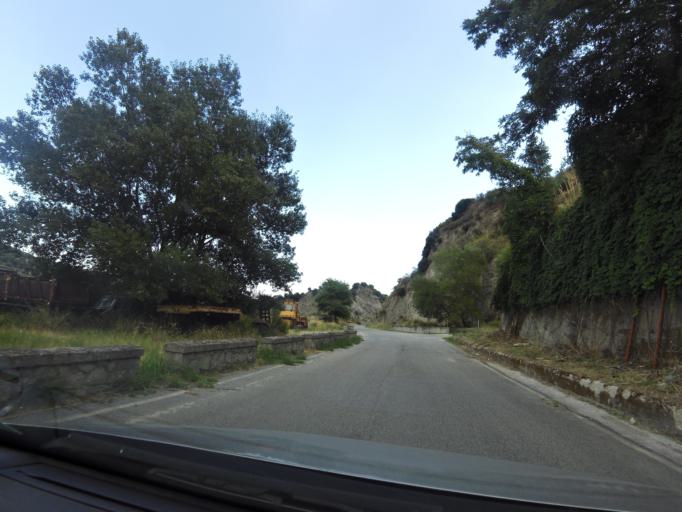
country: IT
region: Calabria
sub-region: Provincia di Reggio Calabria
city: Stilo
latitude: 38.4651
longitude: 16.4899
